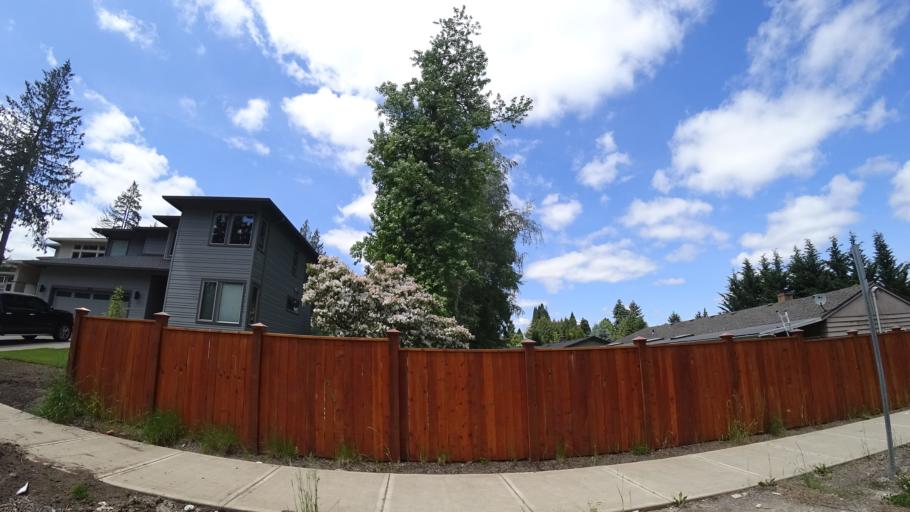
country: US
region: Oregon
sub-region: Washington County
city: King City
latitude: 45.4273
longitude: -122.8059
